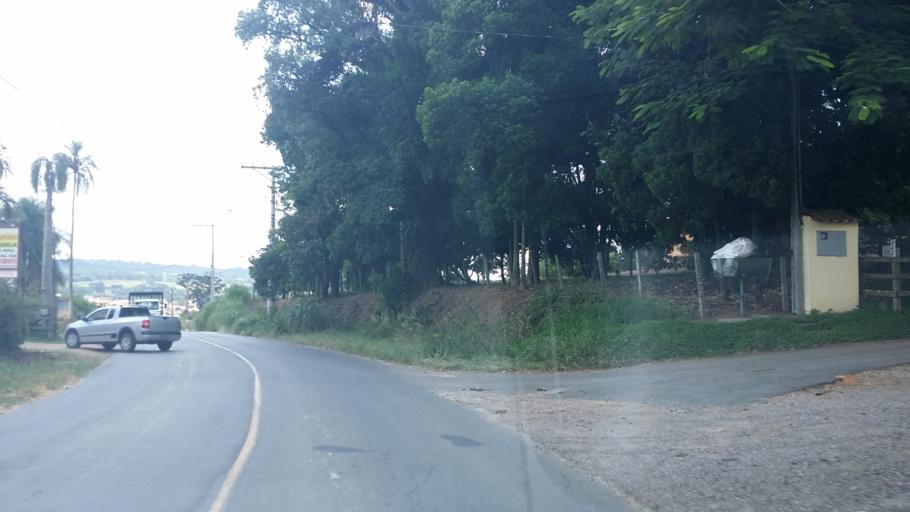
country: BR
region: Sao Paulo
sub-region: Itupeva
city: Itupeva
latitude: -23.1793
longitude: -47.0438
